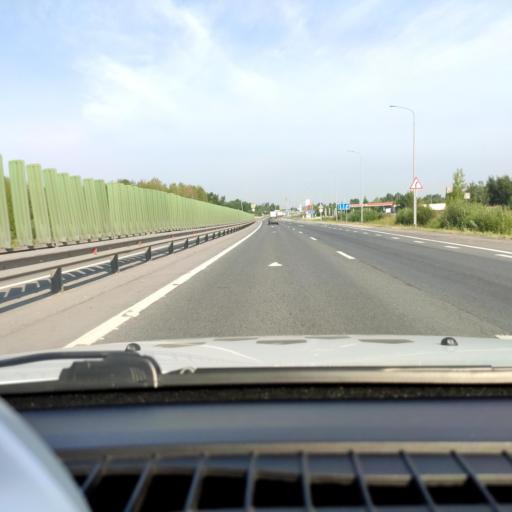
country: RU
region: Perm
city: Overyata
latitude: 58.0518
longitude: 55.8554
